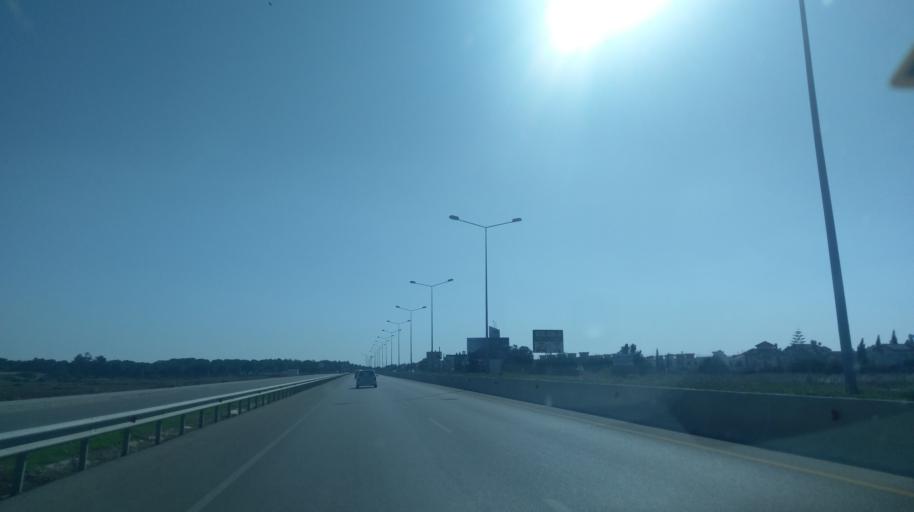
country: CY
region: Ammochostos
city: Trikomo
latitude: 35.2092
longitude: 33.8937
